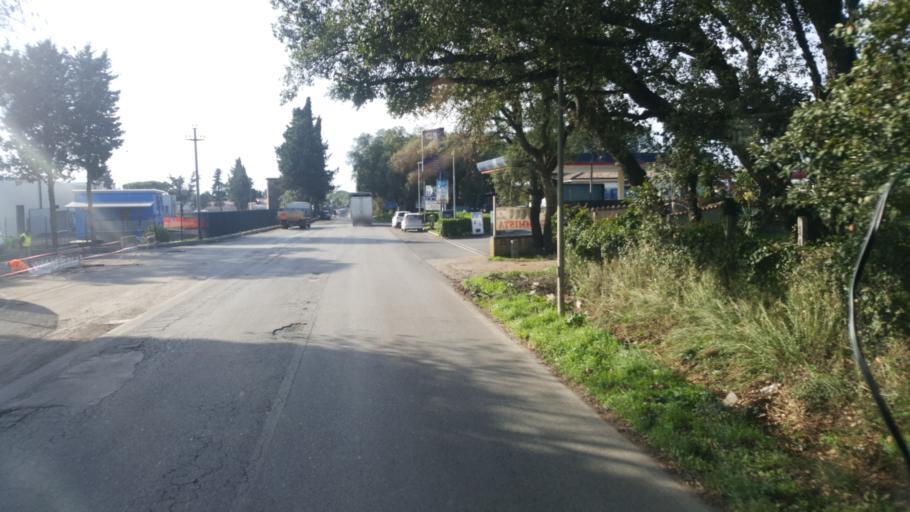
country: IT
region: Latium
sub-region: Provincia di Latina
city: Casalazzara
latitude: 41.6252
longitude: 12.5868
